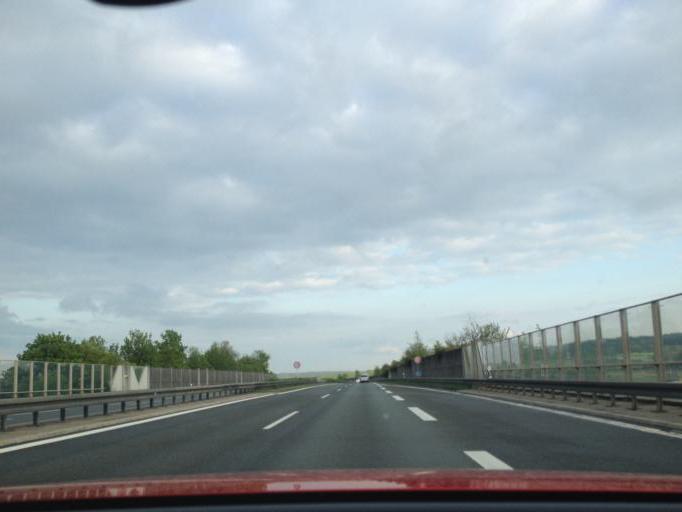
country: DE
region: Bavaria
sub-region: Upper Palatinate
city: Weiden
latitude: 49.6723
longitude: 12.1321
